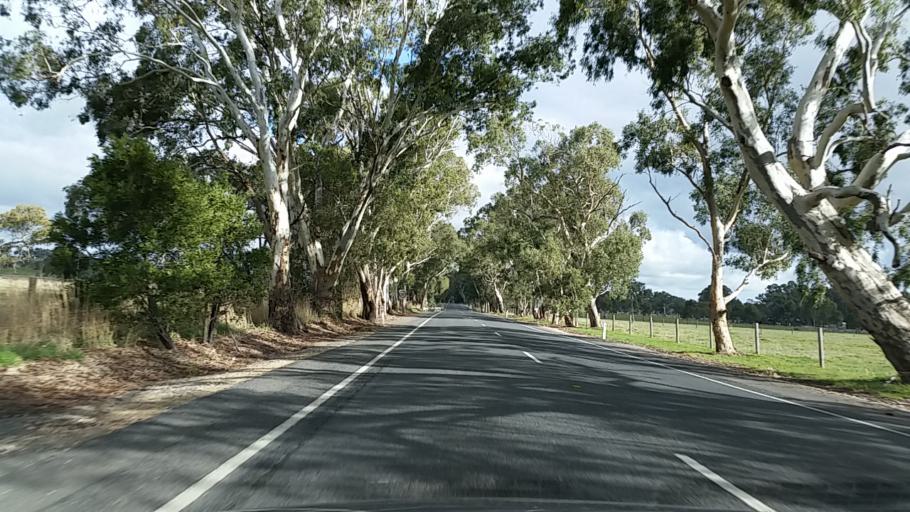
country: AU
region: South Australia
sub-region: Mount Barker
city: Meadows
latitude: -35.1859
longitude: 138.7357
